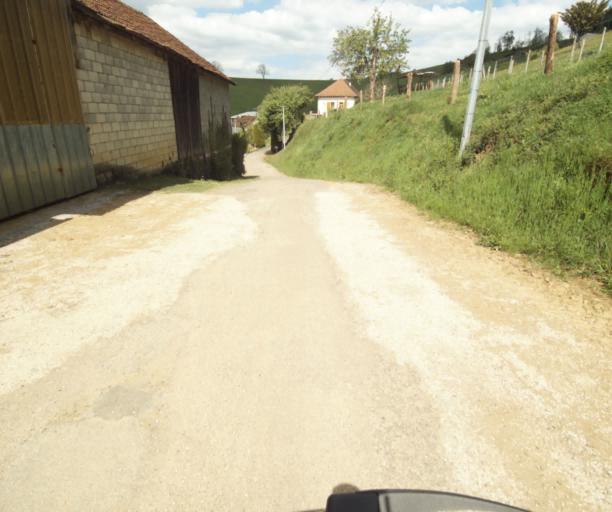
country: FR
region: Limousin
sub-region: Departement de la Correze
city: Naves
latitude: 45.2924
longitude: 1.7670
